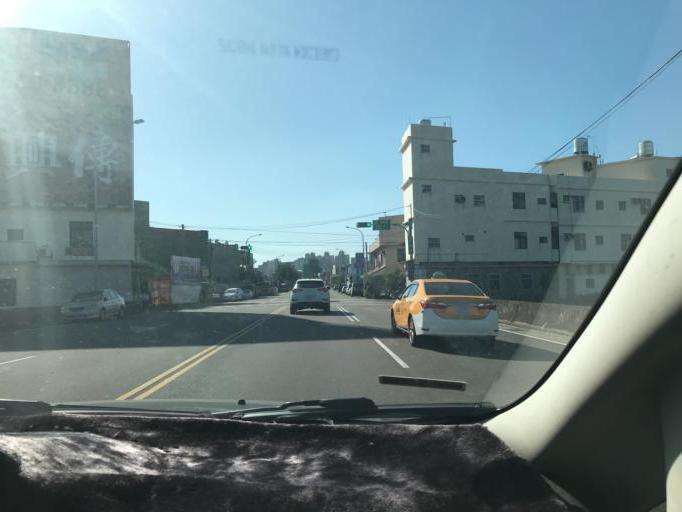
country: TW
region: Taiwan
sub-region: Hsinchu
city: Hsinchu
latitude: 24.8176
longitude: 120.9889
